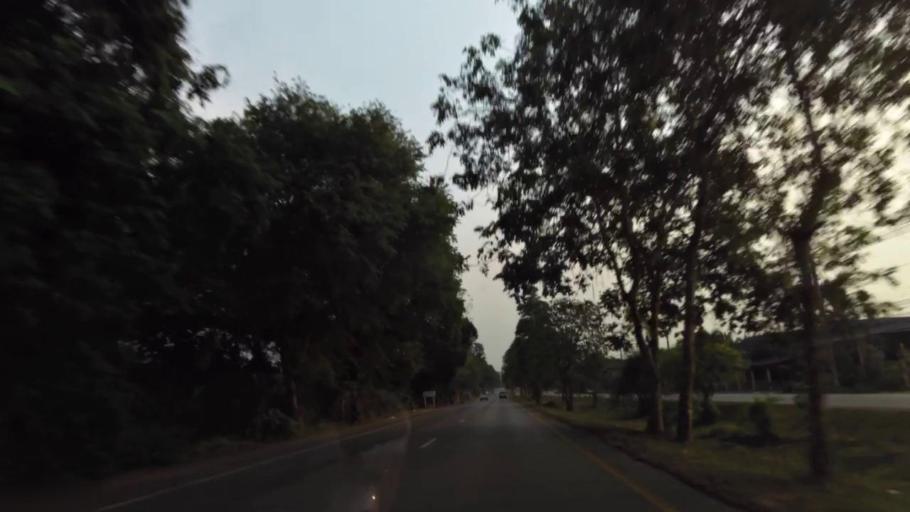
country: TH
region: Chanthaburi
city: Khlung
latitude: 12.4935
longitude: 102.1732
